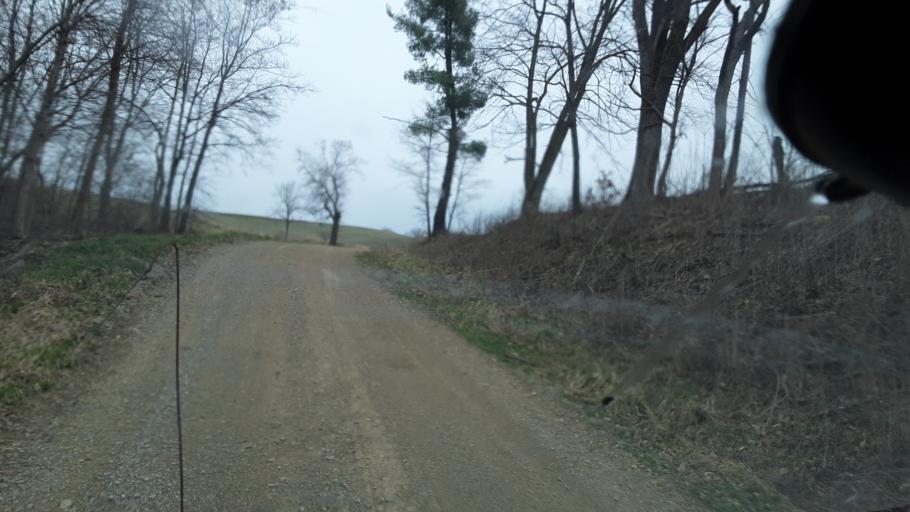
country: US
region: Ohio
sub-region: Coshocton County
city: West Lafayette
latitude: 40.3366
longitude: -81.6956
